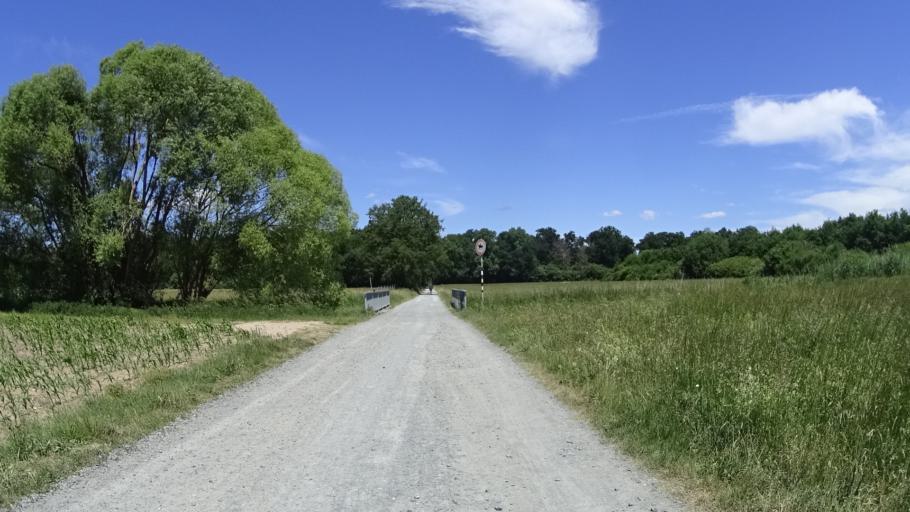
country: DE
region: Hesse
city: Weiterstadt
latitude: 49.9468
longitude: 8.5581
